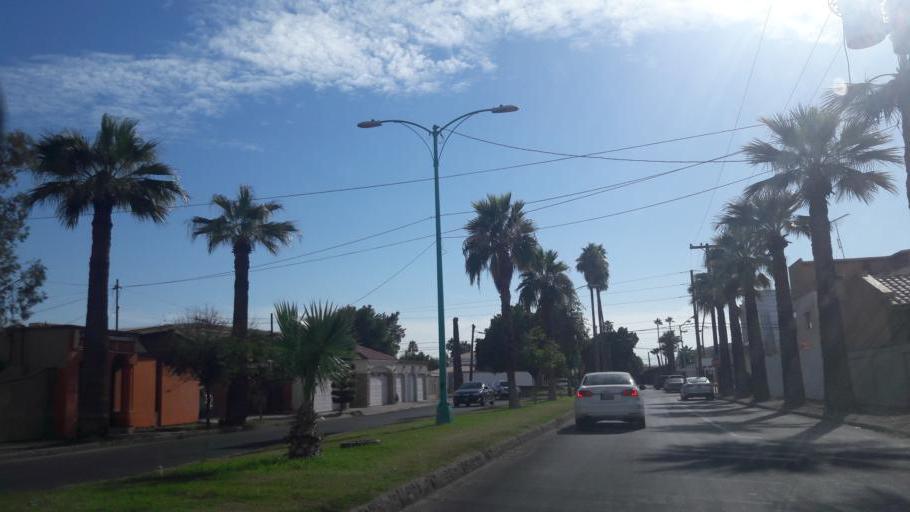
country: MX
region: Baja California
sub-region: Mexicali
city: Mexicali
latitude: 32.6496
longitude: -115.4506
